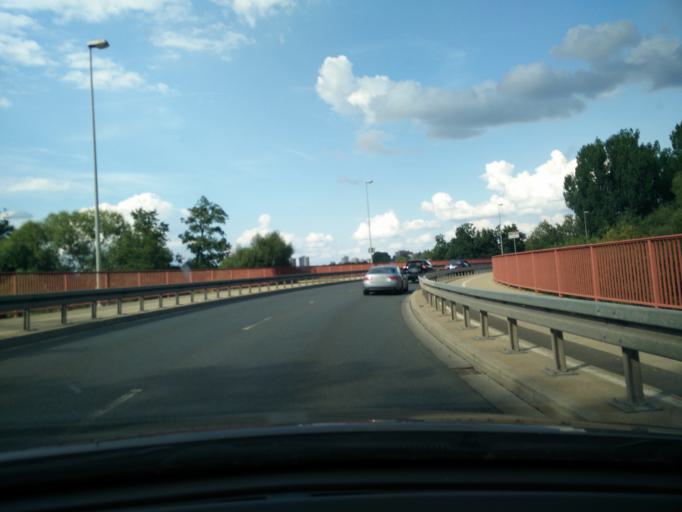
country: DE
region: Bavaria
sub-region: Regierungsbezirk Mittelfranken
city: Stein
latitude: 49.3770
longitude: 11.0255
